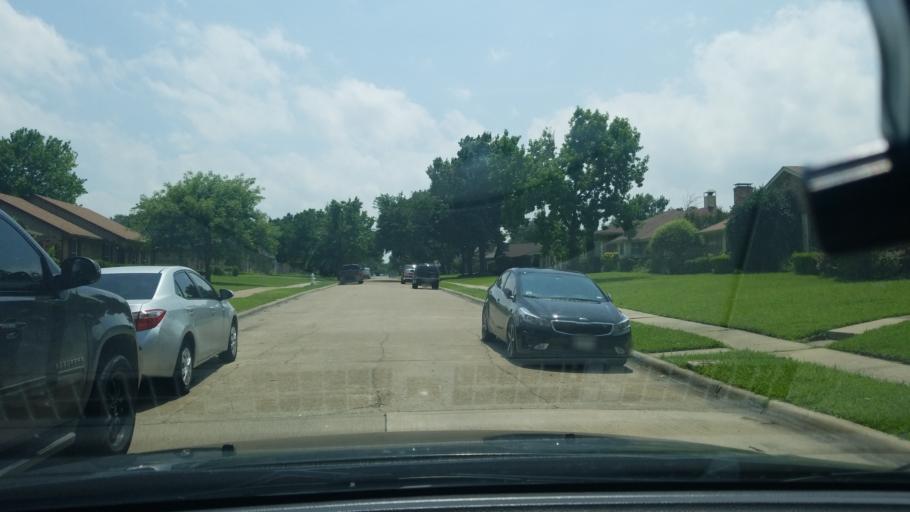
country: US
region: Texas
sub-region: Dallas County
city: Mesquite
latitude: 32.8109
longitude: -96.6441
